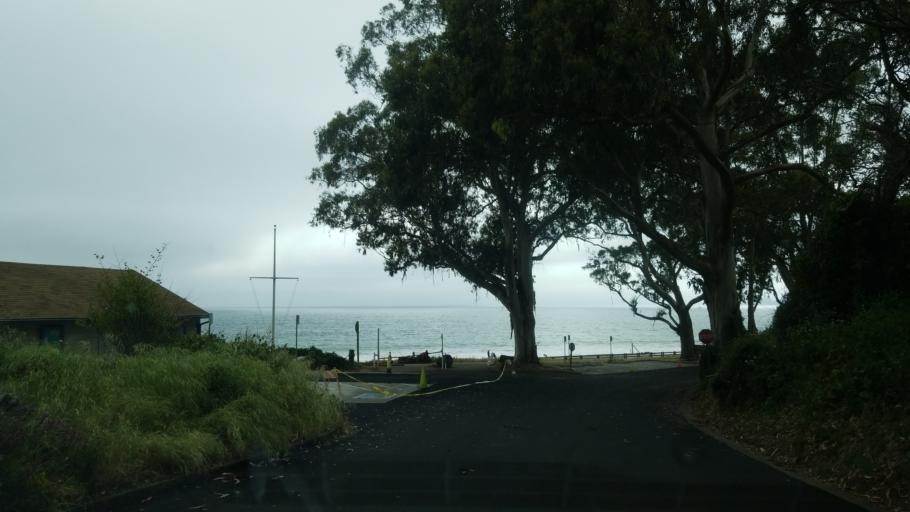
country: US
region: California
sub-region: Santa Cruz County
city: Seacliff
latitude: 36.9728
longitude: -121.9135
